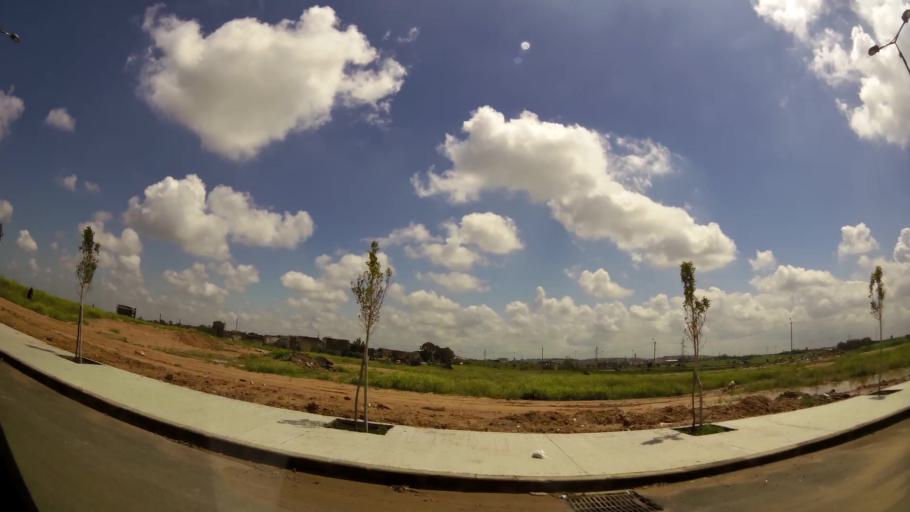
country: MA
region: Grand Casablanca
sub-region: Mediouna
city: Tit Mellil
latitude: 33.5396
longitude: -7.5452
